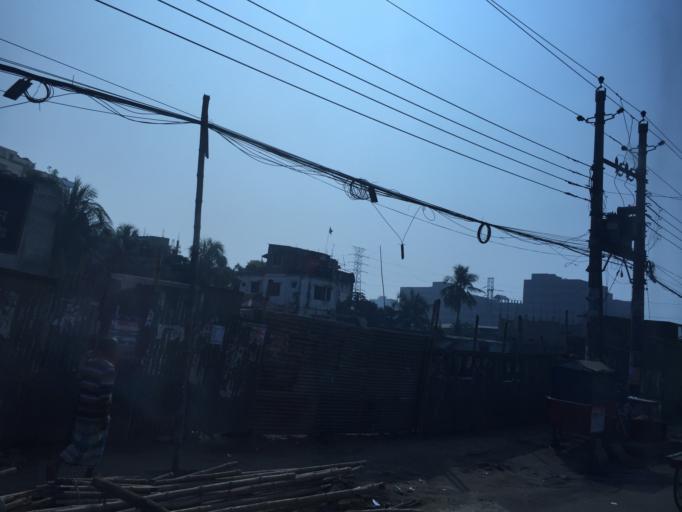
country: BD
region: Dhaka
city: Paltan
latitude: 23.7716
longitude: 90.4254
